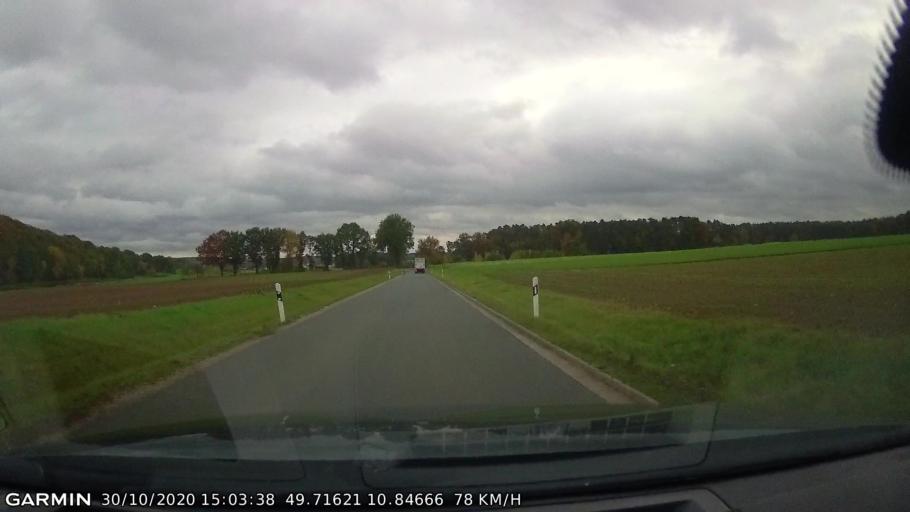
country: DE
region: Bavaria
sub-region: Regierungsbezirk Mittelfranken
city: Gremsdorf
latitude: 49.7161
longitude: 10.8467
